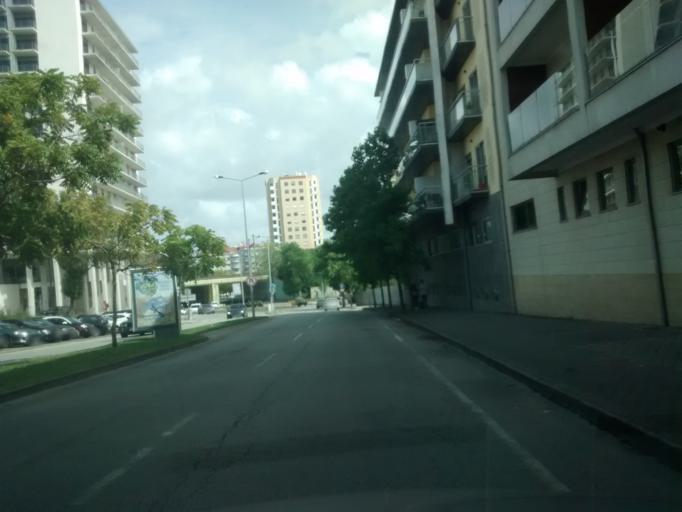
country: PT
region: Aveiro
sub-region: Aveiro
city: Aveiro
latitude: 40.6413
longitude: -8.6437
